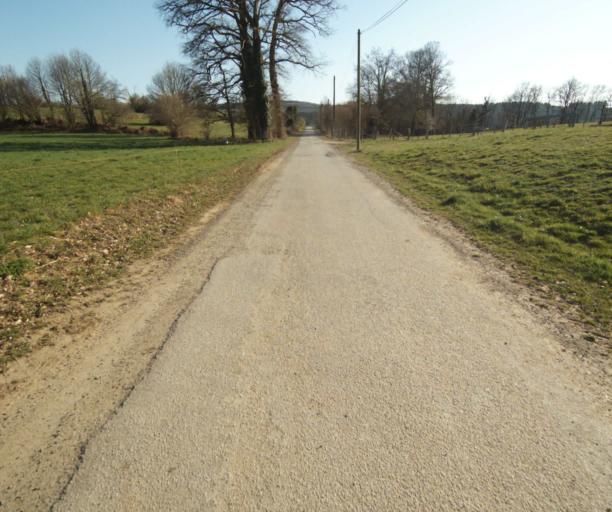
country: FR
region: Limousin
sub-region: Departement de la Correze
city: Chamboulive
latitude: 45.5013
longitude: 1.7257
